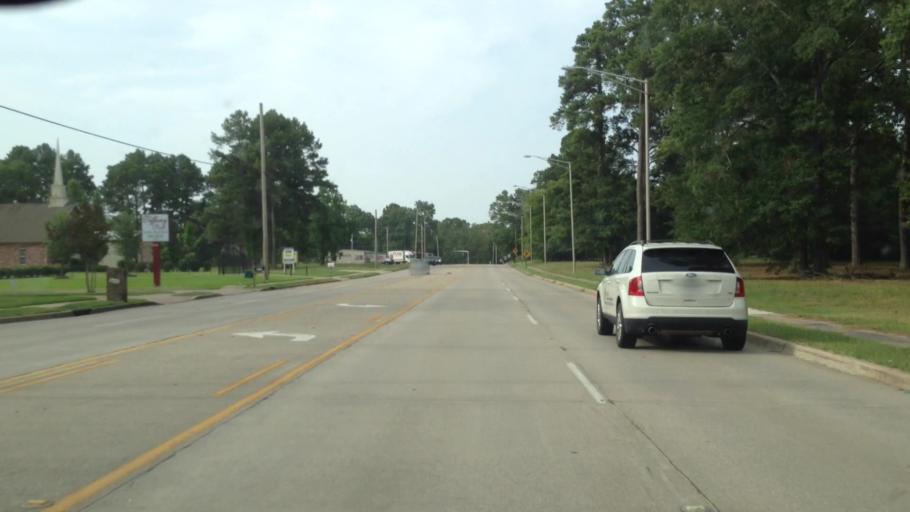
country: US
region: Louisiana
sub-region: De Soto Parish
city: Stonewall
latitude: 32.3974
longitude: -93.8147
